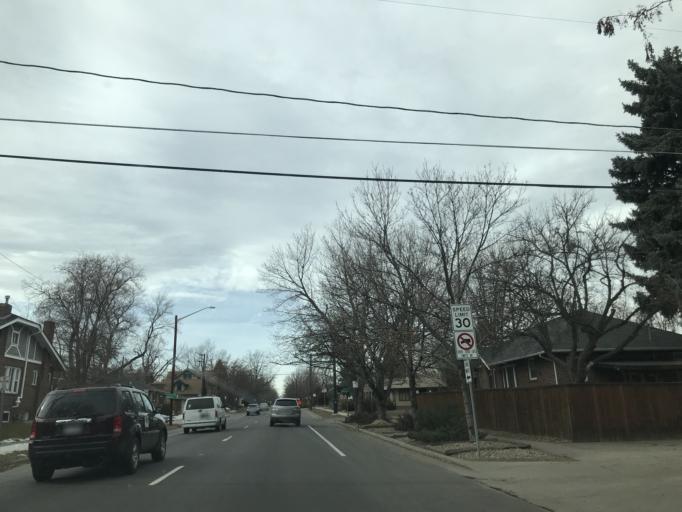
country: US
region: Colorado
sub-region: Arapahoe County
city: Glendale
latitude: 39.7292
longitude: -104.9444
